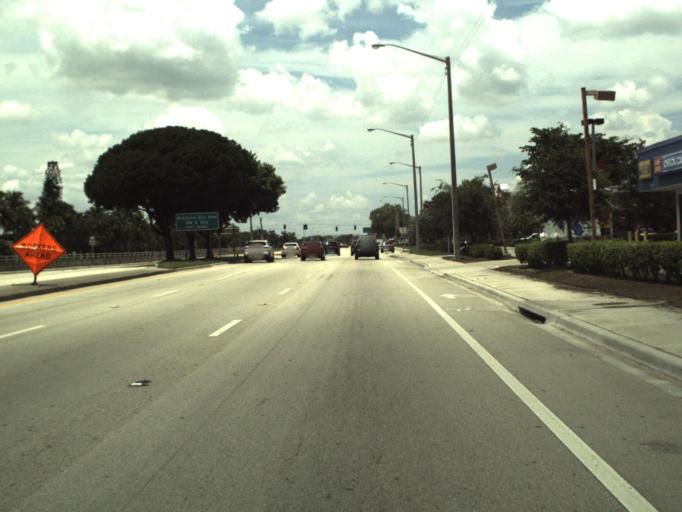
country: US
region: Florida
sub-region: Broward County
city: Pompano Beach
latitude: 26.2317
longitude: -80.1275
